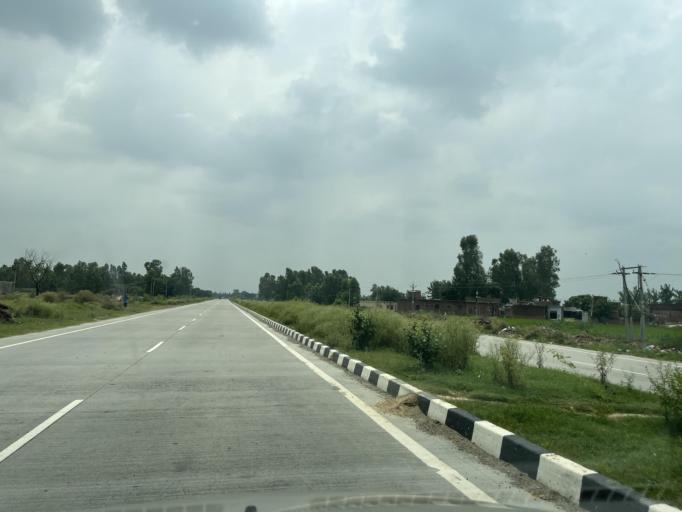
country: IN
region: Uttar Pradesh
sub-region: Bijnor
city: Najibabad
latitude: 29.5580
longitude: 78.3390
